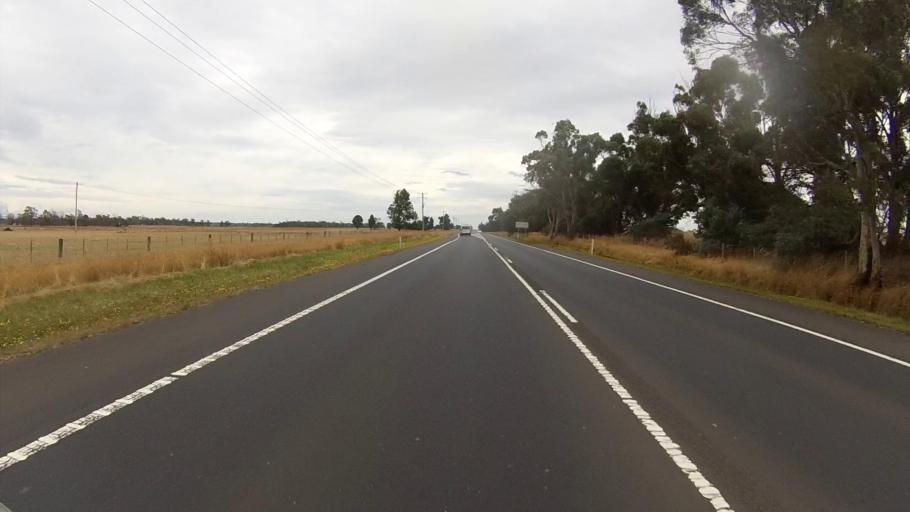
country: AU
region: Tasmania
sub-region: Northern Midlands
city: Evandale
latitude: -41.6884
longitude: 147.2796
